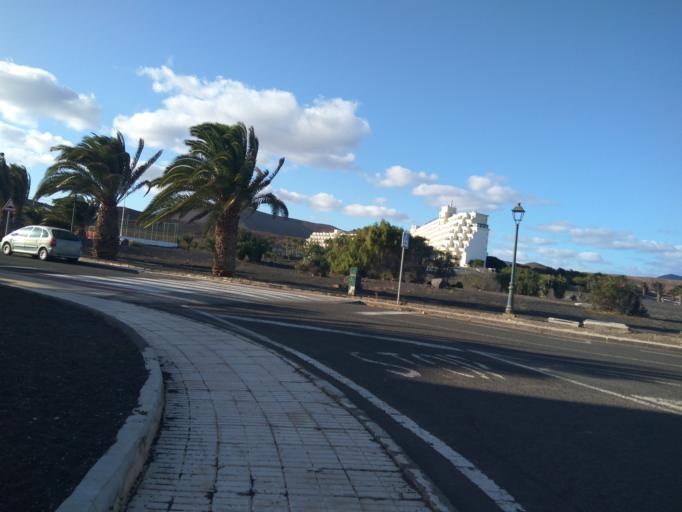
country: ES
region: Canary Islands
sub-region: Provincia de Las Palmas
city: Arrecife
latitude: 29.0072
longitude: -13.4877
